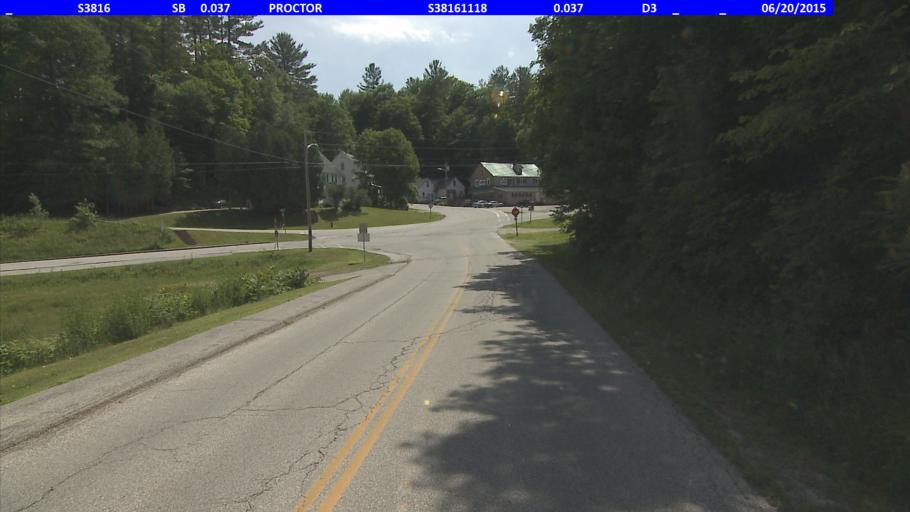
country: US
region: Vermont
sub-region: Rutland County
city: West Rutland
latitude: 43.6636
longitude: -73.0393
